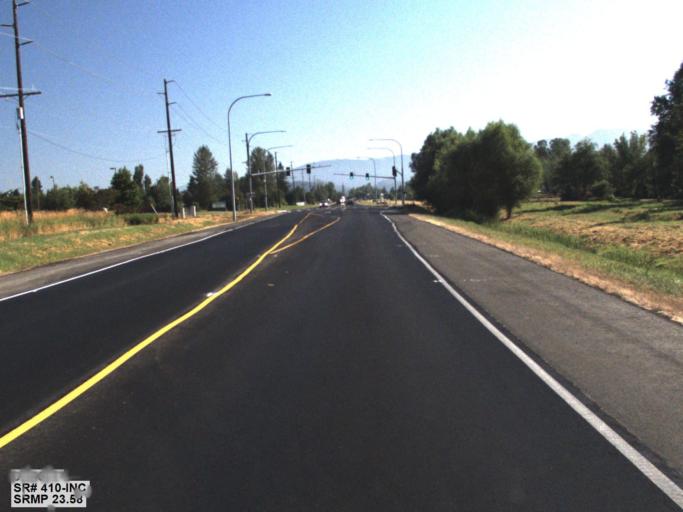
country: US
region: Washington
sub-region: King County
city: Enumclaw
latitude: 47.1909
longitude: -122.0015
